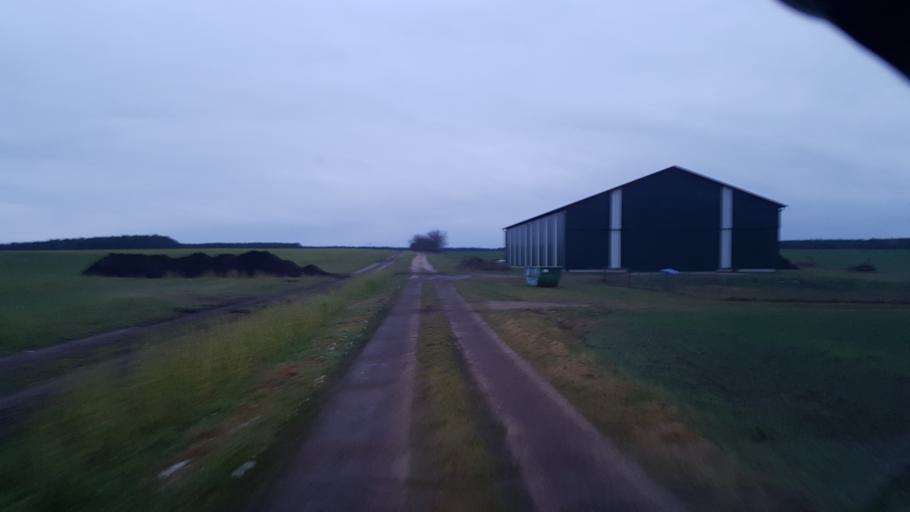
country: DE
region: Brandenburg
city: Tauche
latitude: 52.0642
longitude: 14.1412
